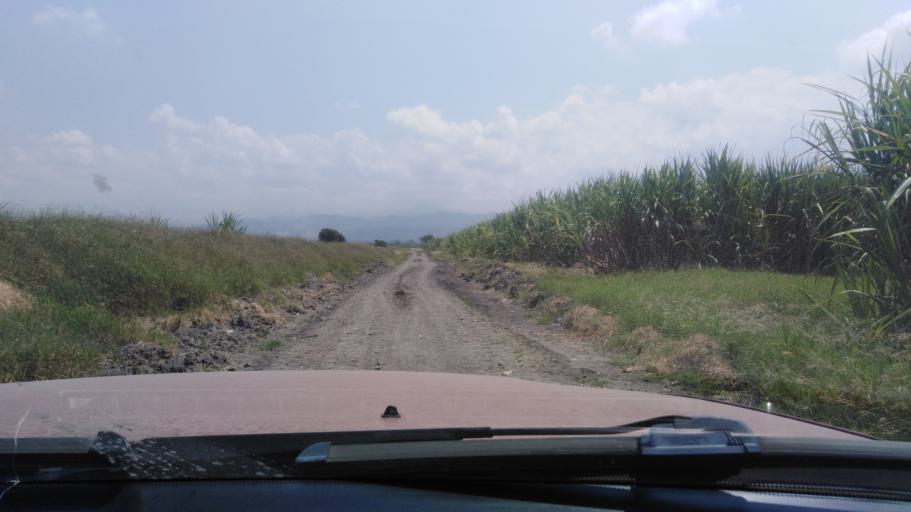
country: CO
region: Valle del Cauca
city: San Pedro
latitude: 3.9993
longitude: -76.2790
